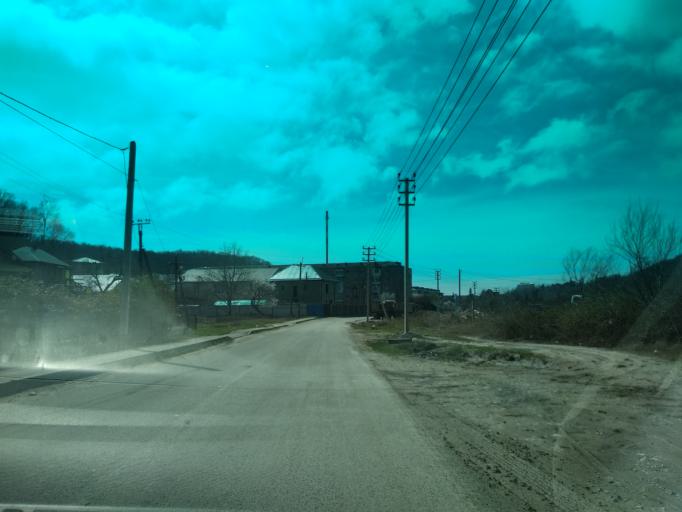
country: RU
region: Krasnodarskiy
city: Shepsi
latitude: 44.0454
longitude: 39.1562
